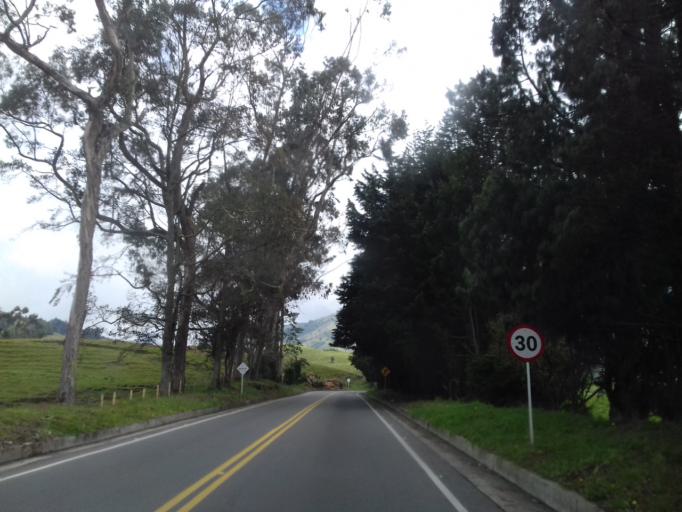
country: CO
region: Caldas
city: Villamaria
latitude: 5.0168
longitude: -75.3564
